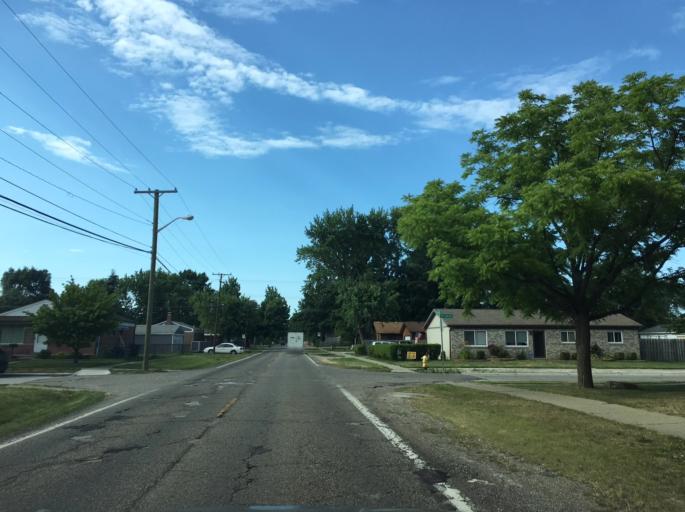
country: US
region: Michigan
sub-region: Macomb County
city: Fraser
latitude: 42.5408
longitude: -82.9196
